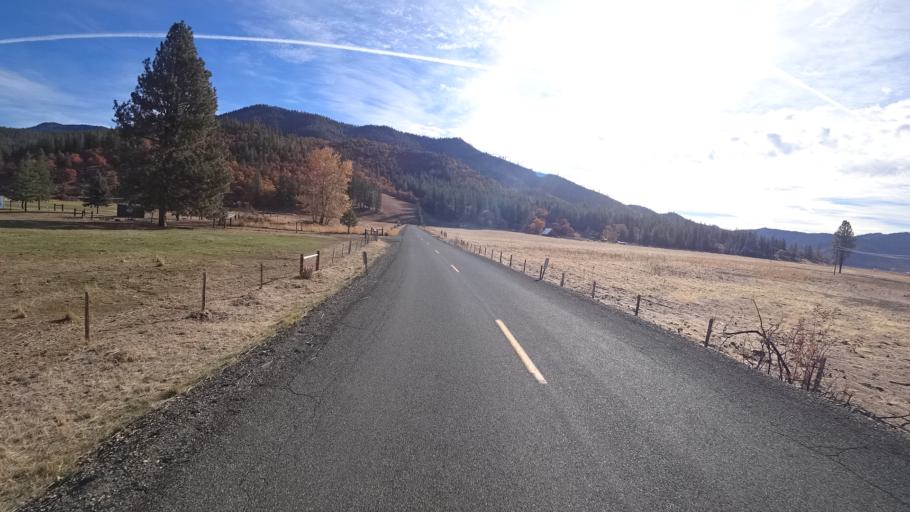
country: US
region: California
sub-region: Siskiyou County
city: Yreka
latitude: 41.6565
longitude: -122.8352
